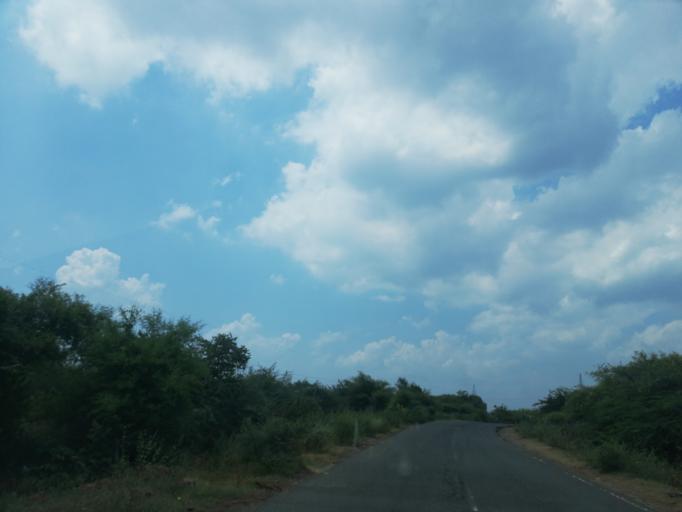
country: IN
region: Andhra Pradesh
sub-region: Guntur
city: Macherla
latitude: 16.5648
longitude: 79.3486
